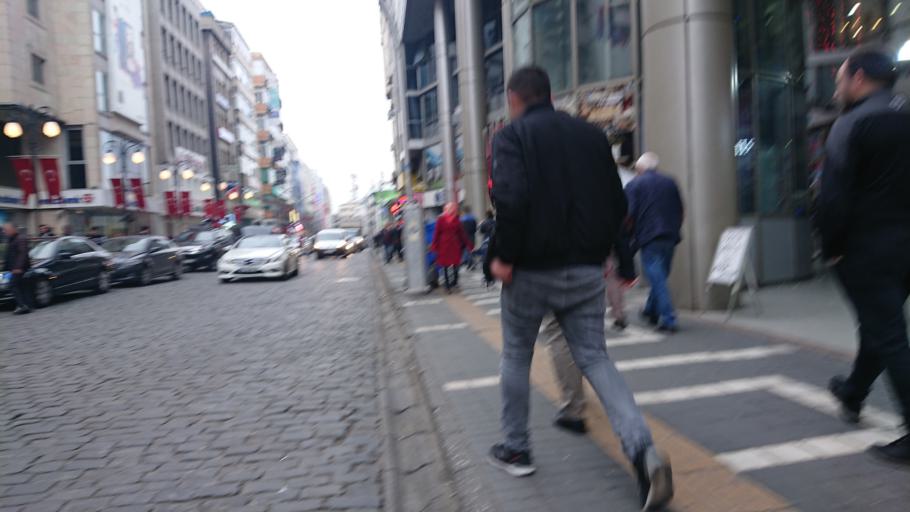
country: TR
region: Trabzon
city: Trabzon
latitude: 41.0056
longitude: 39.7291
